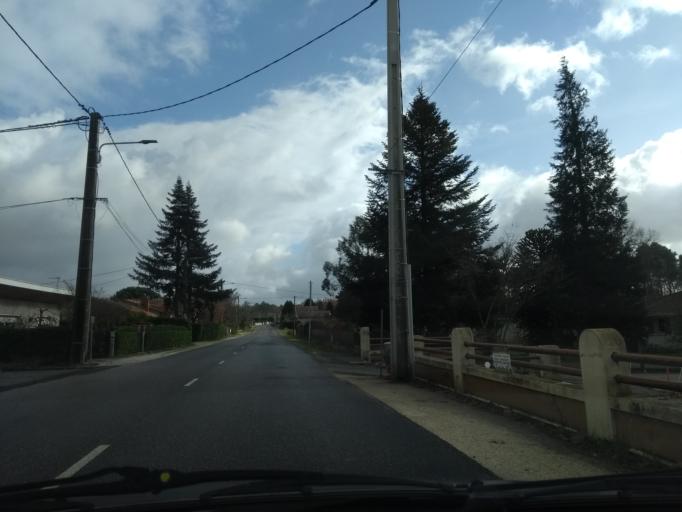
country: FR
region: Aquitaine
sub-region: Departement de la Gironde
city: Belin-Beliet
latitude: 44.4928
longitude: -0.7880
